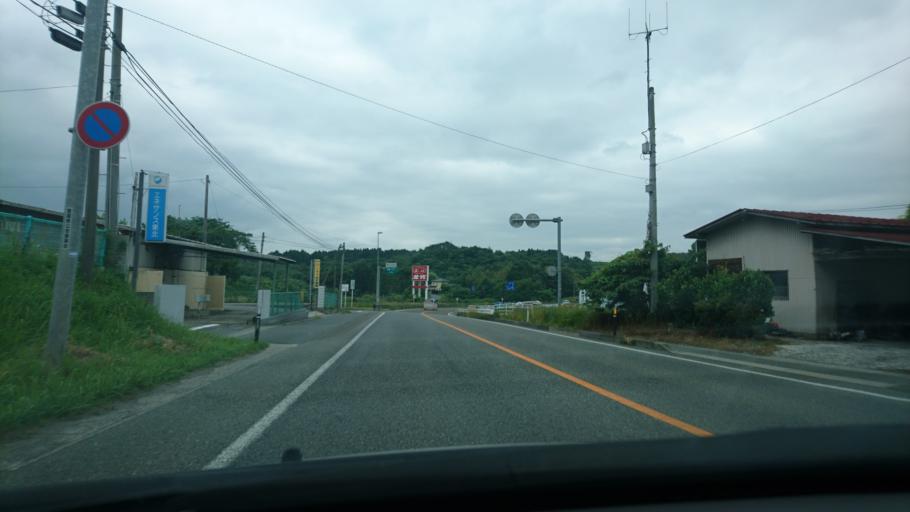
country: JP
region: Miyagi
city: Furukawa
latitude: 38.7232
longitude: 141.0230
